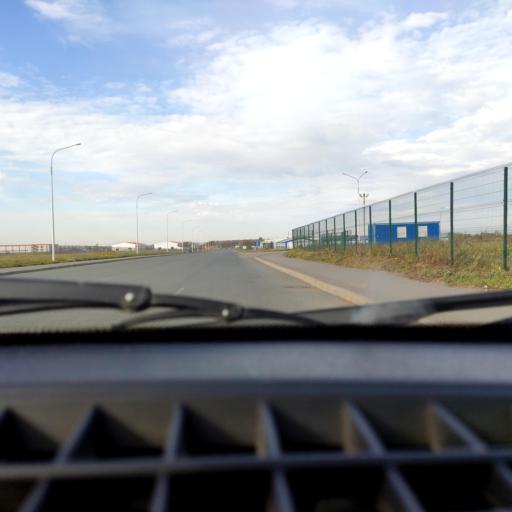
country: RU
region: Bashkortostan
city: Ufa
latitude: 54.6021
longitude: 55.9143
